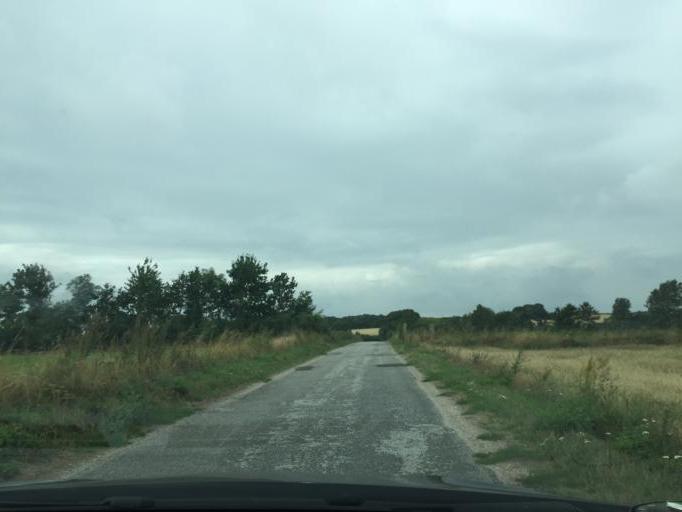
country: DK
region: South Denmark
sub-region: Assens Kommune
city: Harby
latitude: 55.2031
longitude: 10.0298
